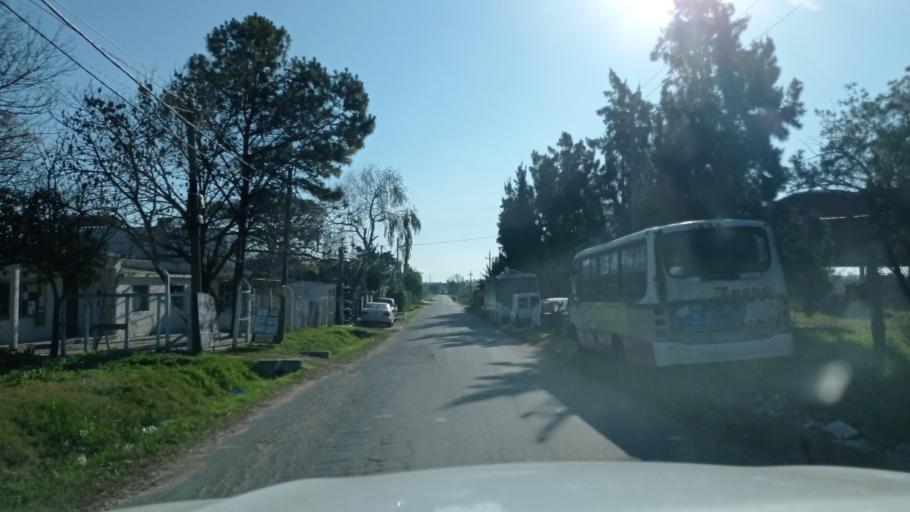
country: UY
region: Canelones
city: La Paz
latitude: -34.8350
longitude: -56.2476
